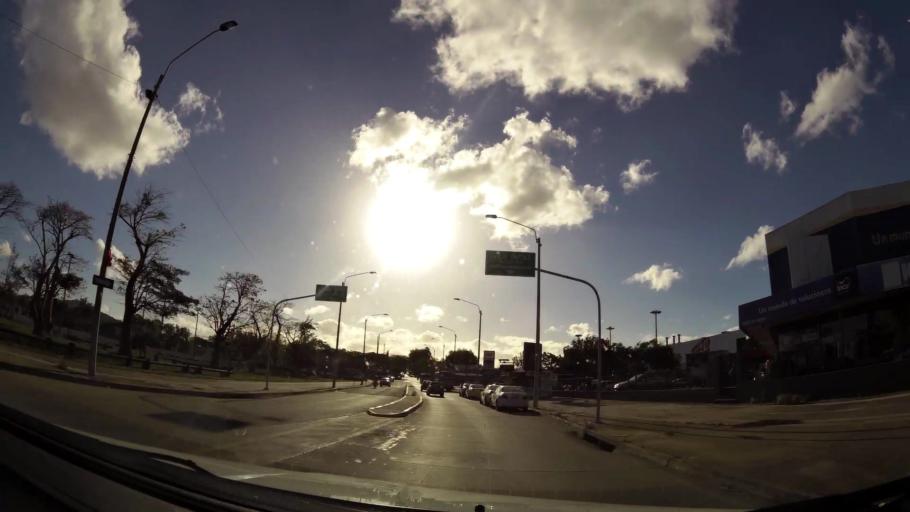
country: UY
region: Montevideo
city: Montevideo
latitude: -34.8735
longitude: -56.2461
